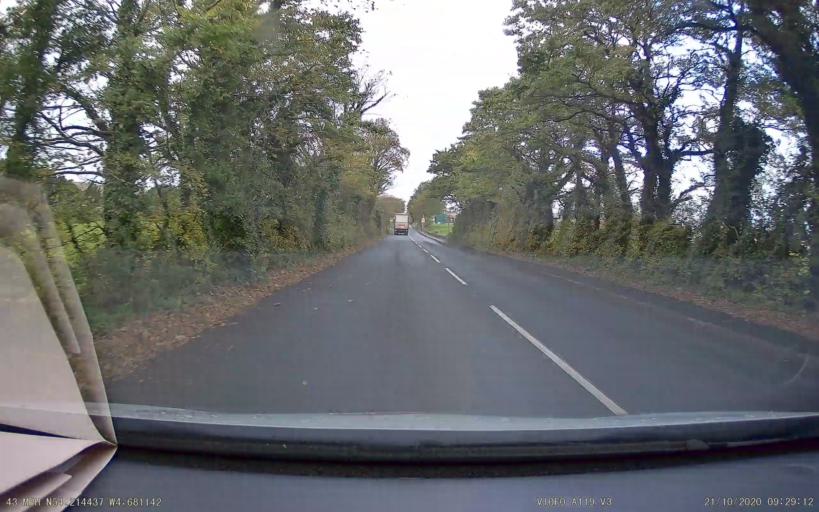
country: IM
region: Castletown
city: Castletown
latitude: 54.0000
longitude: -4.6811
